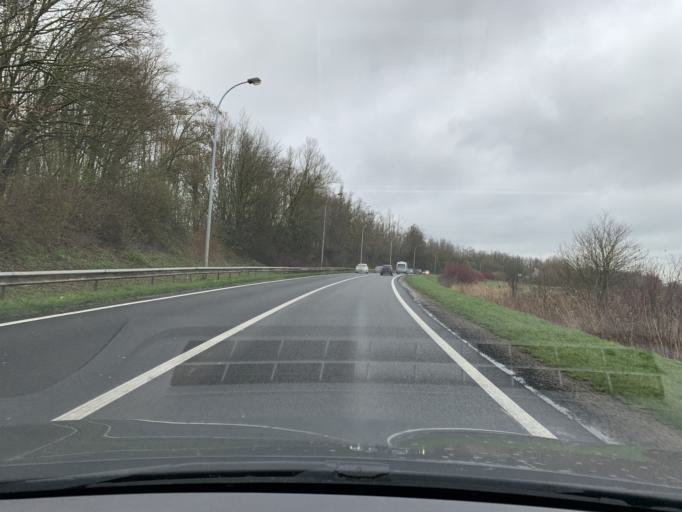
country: FR
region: Nord-Pas-de-Calais
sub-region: Departement du Nord
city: Sin-le-Noble
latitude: 50.3705
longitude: 3.1205
